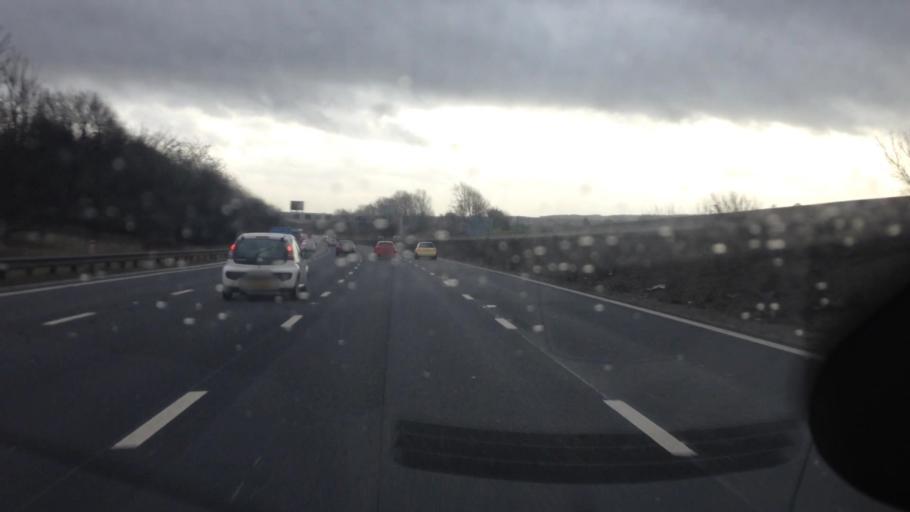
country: GB
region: England
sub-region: City and Borough of Wakefield
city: Horbury
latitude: 53.6736
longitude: -1.5506
